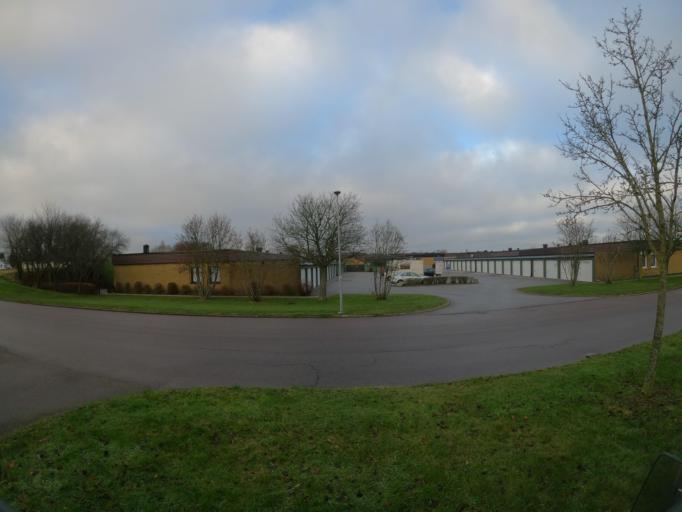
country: SE
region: Skane
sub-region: Svedala Kommun
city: Svedala
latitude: 55.5141
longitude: 13.2233
